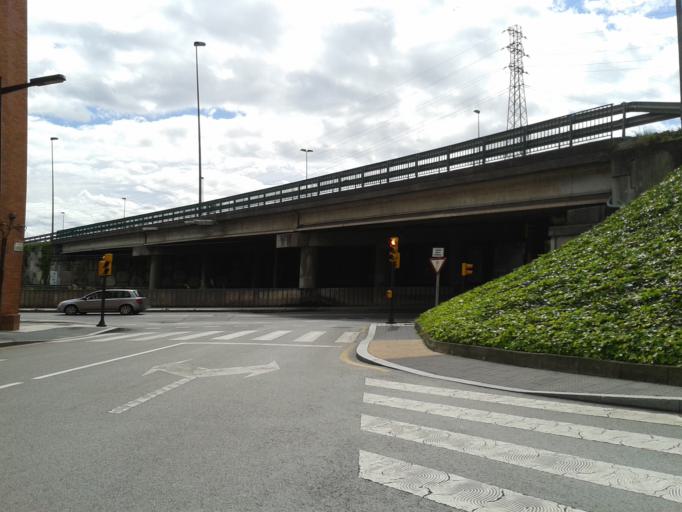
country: ES
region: Asturias
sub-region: Province of Asturias
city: Natahoyo
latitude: 43.5366
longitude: -5.6896
